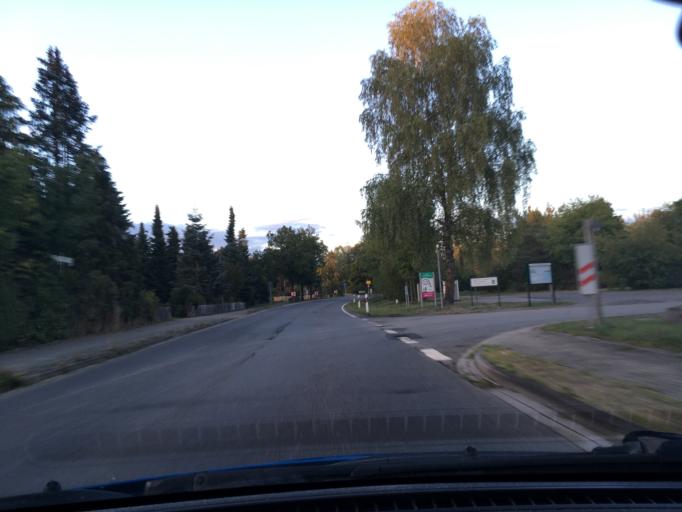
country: DE
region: Lower Saxony
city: Fassberg
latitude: 52.8786
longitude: 10.1245
